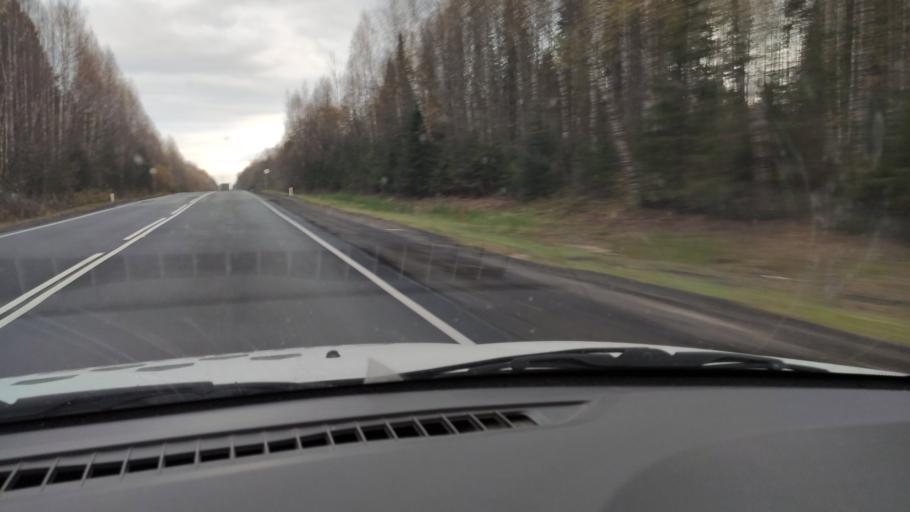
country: RU
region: Kirov
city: Omutninsk
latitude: 58.7645
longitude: 51.9893
